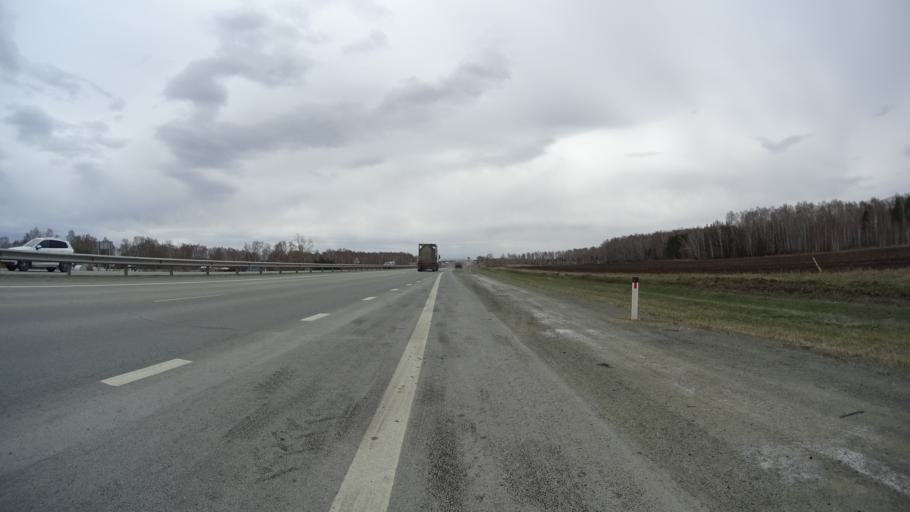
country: RU
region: Chelyabinsk
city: Yemanzhelinka
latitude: 54.8216
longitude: 61.3090
